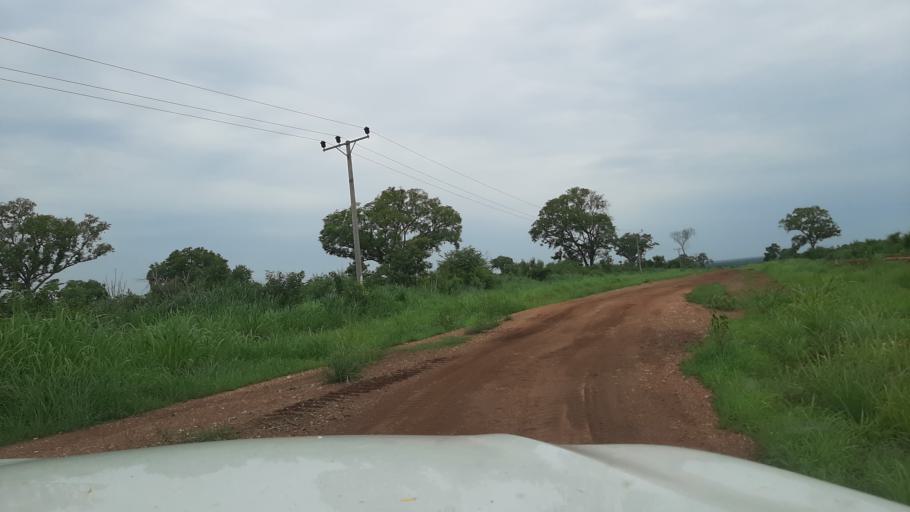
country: ET
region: Gambela
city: Gambela
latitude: 8.1781
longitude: 34.4904
